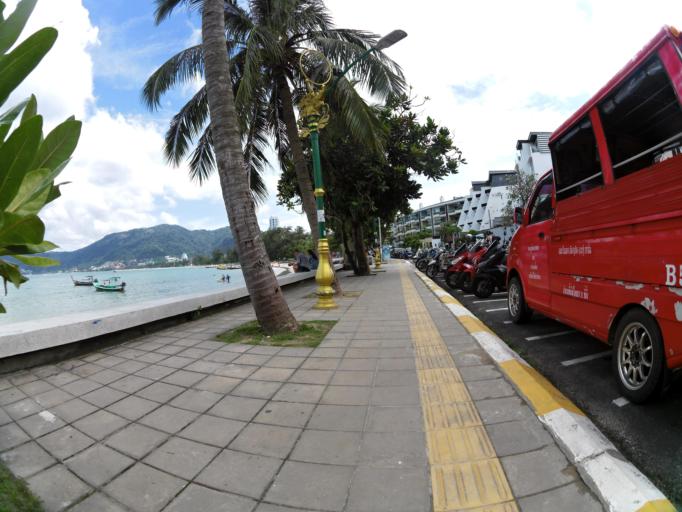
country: TH
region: Phuket
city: Patong
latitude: 7.8862
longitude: 98.2893
